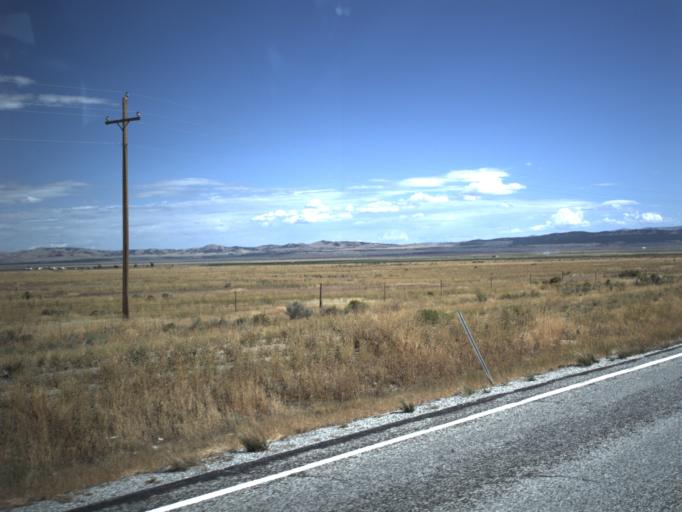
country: US
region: Idaho
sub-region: Oneida County
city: Malad City
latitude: 41.9661
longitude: -112.9643
